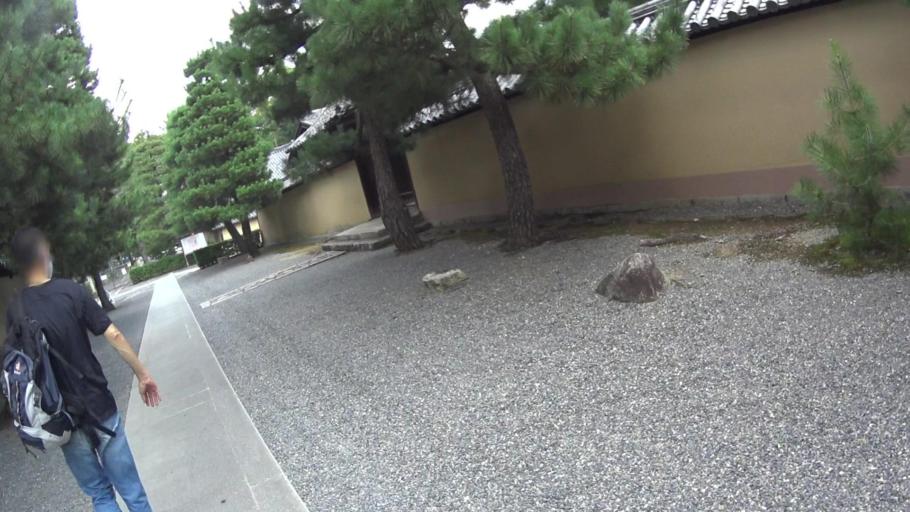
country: JP
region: Kyoto
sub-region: Kyoto-shi
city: Kamigyo-ku
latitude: 35.0441
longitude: 135.7456
